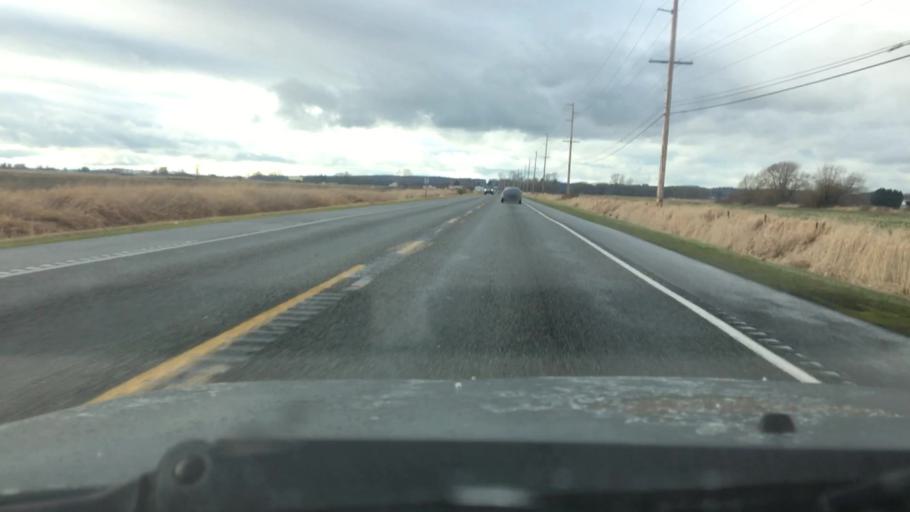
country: US
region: Washington
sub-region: Whatcom County
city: Ferndale
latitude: 48.8191
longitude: -122.5845
